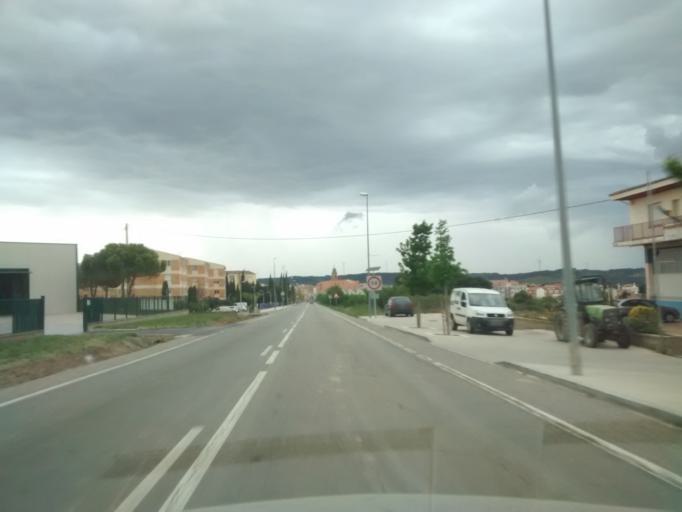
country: ES
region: Catalonia
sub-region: Provincia de Tarragona
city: Gandesa
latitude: 41.0490
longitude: 0.4459
